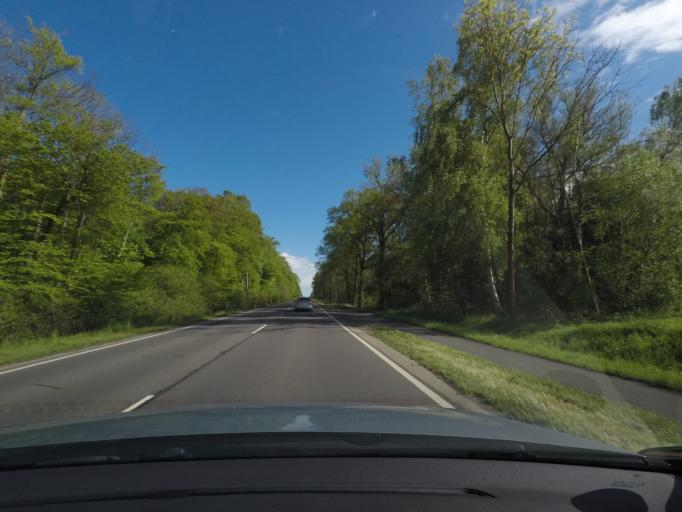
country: DE
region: Lower Saxony
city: Mariental
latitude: 52.2696
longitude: 10.9815
